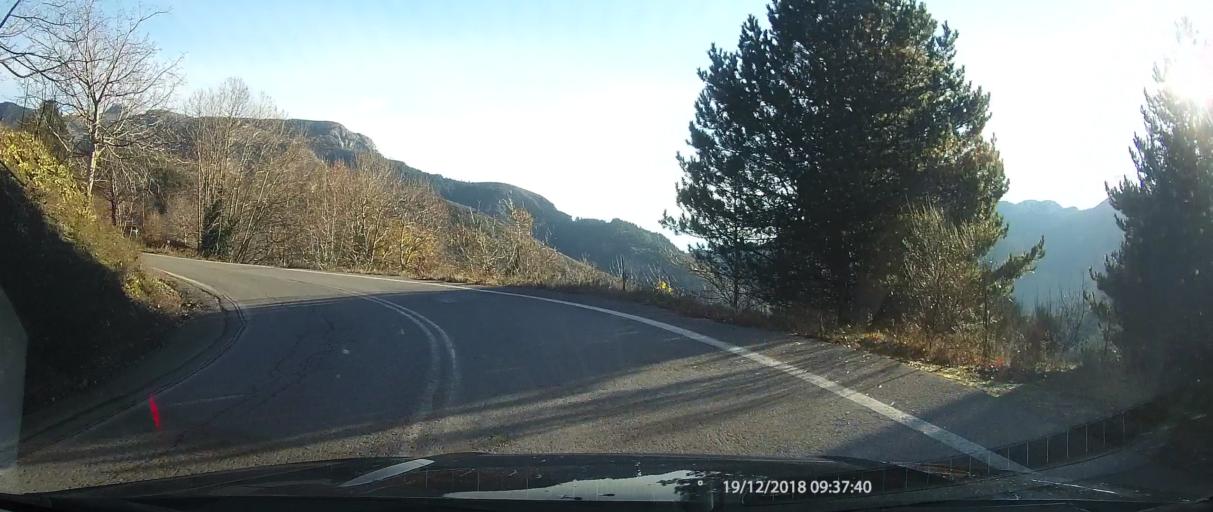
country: GR
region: Peloponnese
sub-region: Nomos Lakonias
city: Magoula
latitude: 37.0809
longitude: 22.2777
